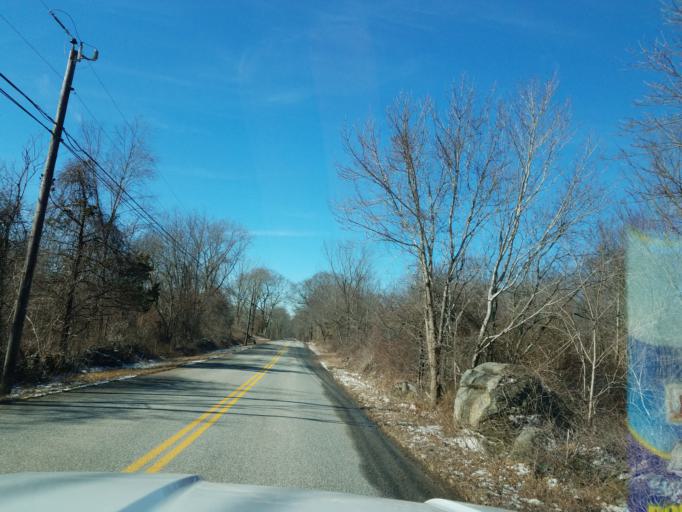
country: US
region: Connecticut
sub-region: New London County
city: Old Mystic
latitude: 41.4545
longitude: -71.9250
